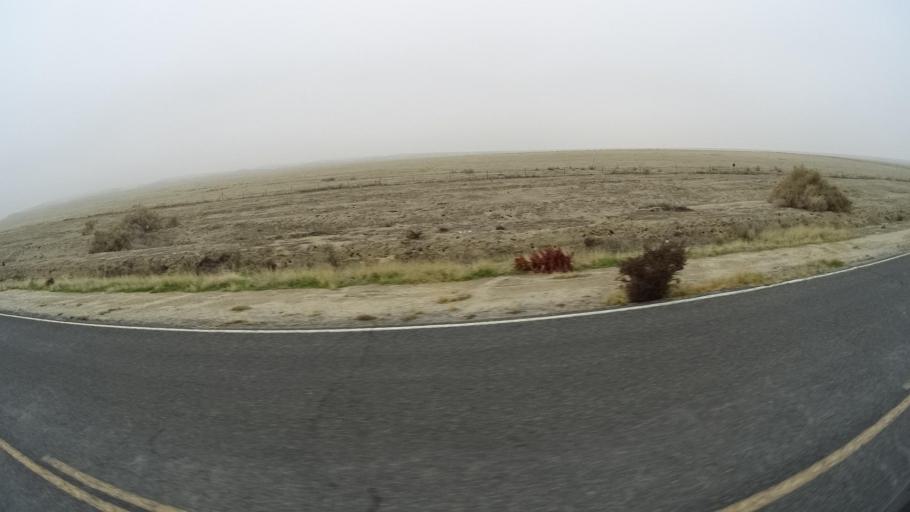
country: US
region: California
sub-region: Kern County
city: Buttonwillow
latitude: 35.3379
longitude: -119.4647
